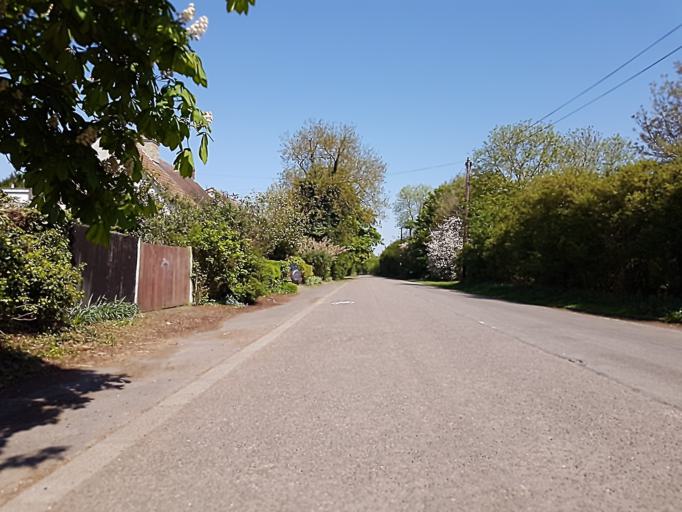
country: GB
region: England
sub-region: Cambridgeshire
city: Melbourn
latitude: 52.1007
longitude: 0.0377
